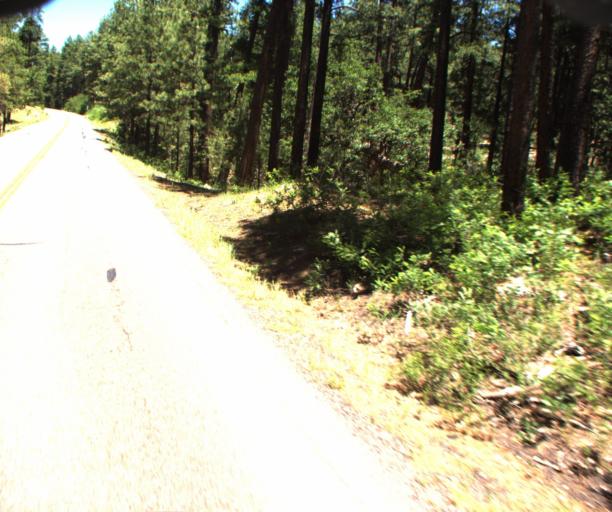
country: US
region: Arizona
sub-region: Gila County
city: Pine
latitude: 34.5095
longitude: -111.3416
